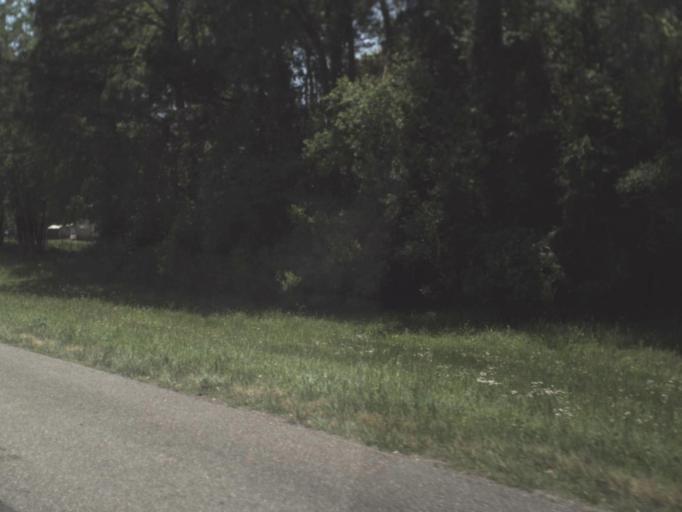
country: US
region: Florida
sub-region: Clay County
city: Bellair-Meadowbrook Terrace
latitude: 30.2633
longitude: -81.7650
